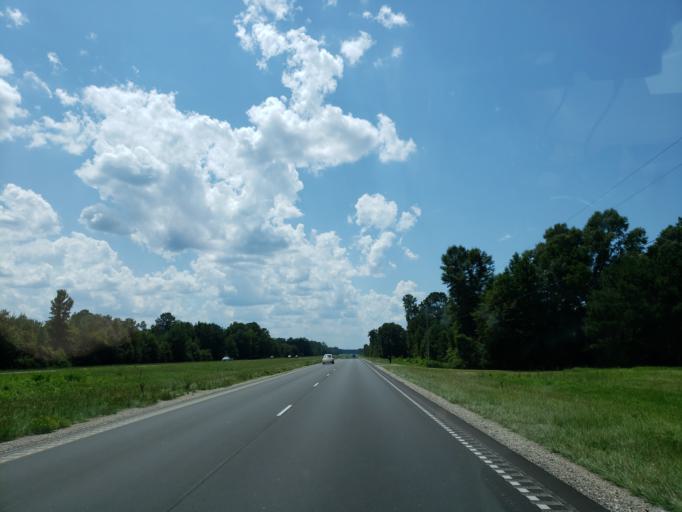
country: US
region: Mississippi
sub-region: Perry County
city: New Augusta
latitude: 31.2077
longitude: -89.0859
